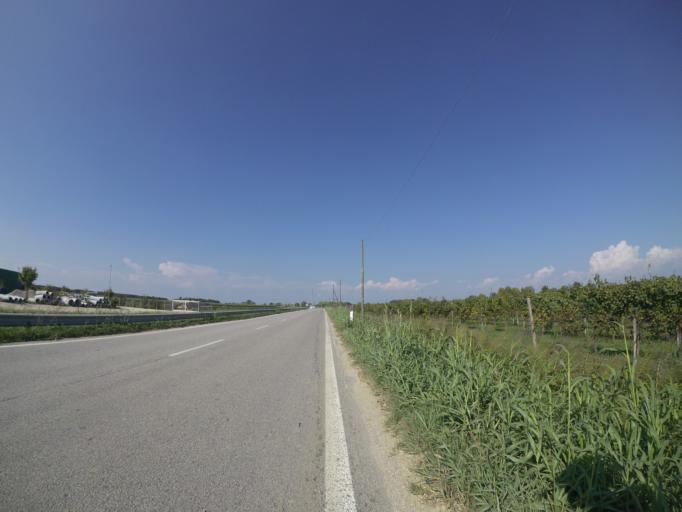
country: IT
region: Friuli Venezia Giulia
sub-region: Provincia di Udine
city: Carlino
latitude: 45.7967
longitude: 13.1660
